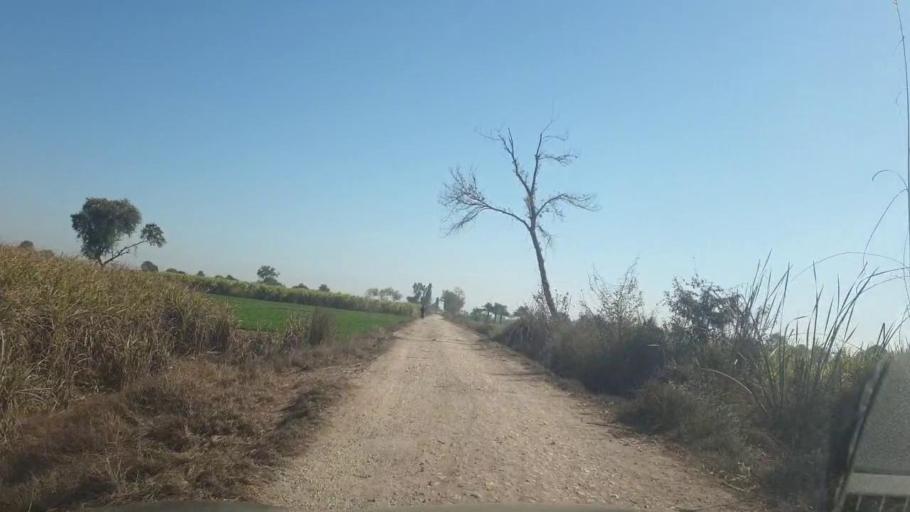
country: PK
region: Sindh
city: Ghotki
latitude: 27.9747
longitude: 69.3338
